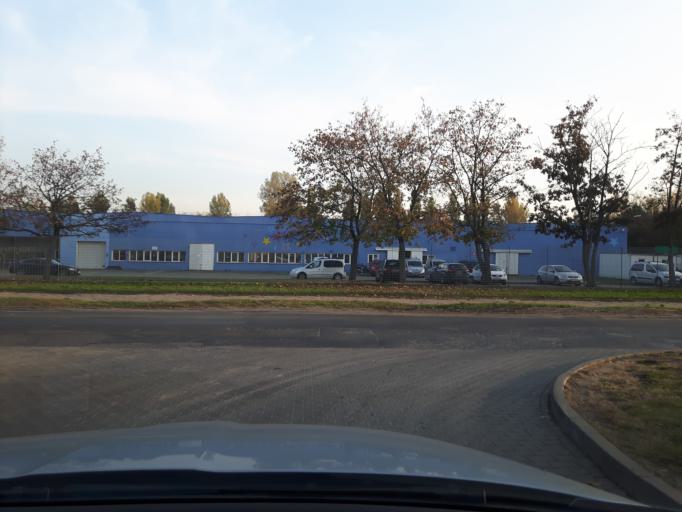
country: PL
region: Masovian Voivodeship
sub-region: Warszawa
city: Praga Poludnie
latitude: 52.2646
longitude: 21.0928
